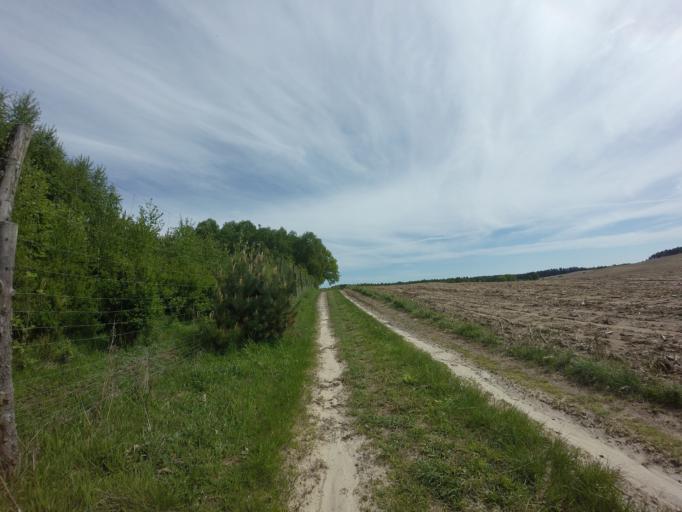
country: PL
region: West Pomeranian Voivodeship
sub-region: Powiat choszczenski
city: Recz
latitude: 53.1581
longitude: 15.5758
